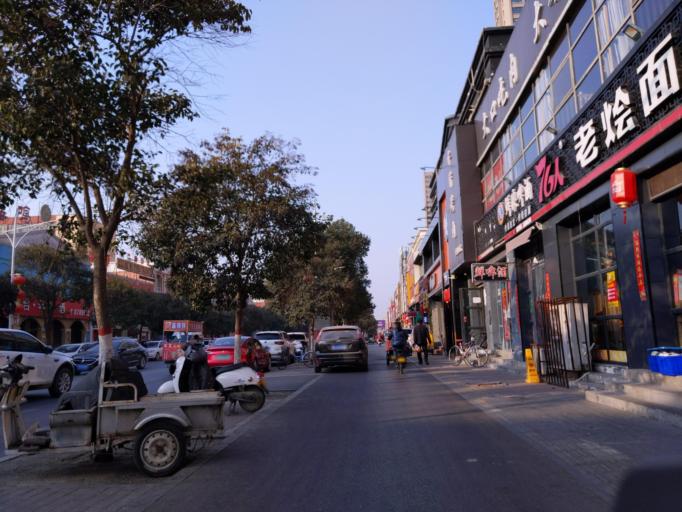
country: CN
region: Henan Sheng
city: Puyang
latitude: 35.7743
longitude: 115.0329
